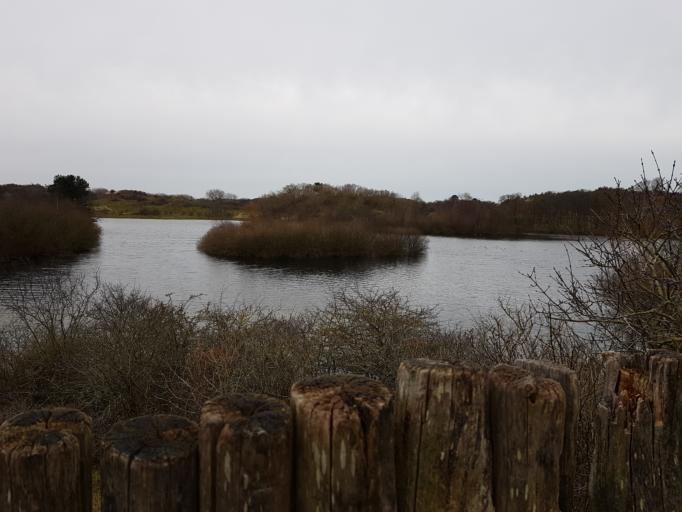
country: NL
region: North Holland
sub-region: Gemeente Bloemendaal
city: Bloemendaal
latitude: 52.3874
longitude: 4.5805
